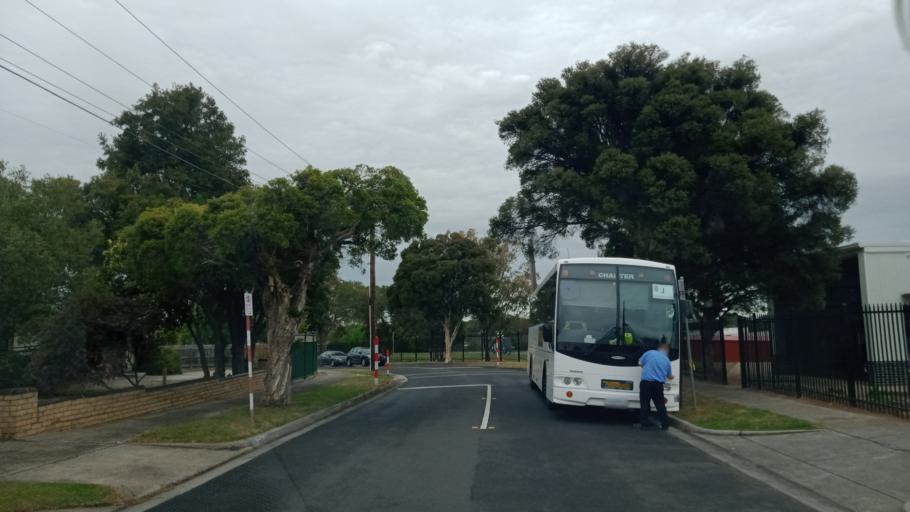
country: AU
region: Victoria
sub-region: Greater Dandenong
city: Springvale
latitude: -37.9397
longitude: 145.1597
